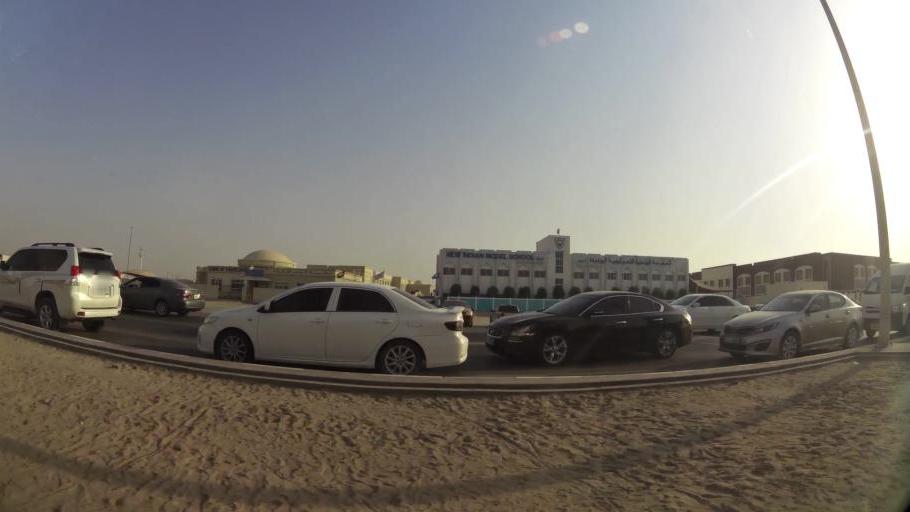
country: AE
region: Ajman
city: Ajman
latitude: 25.3804
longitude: 55.4501
